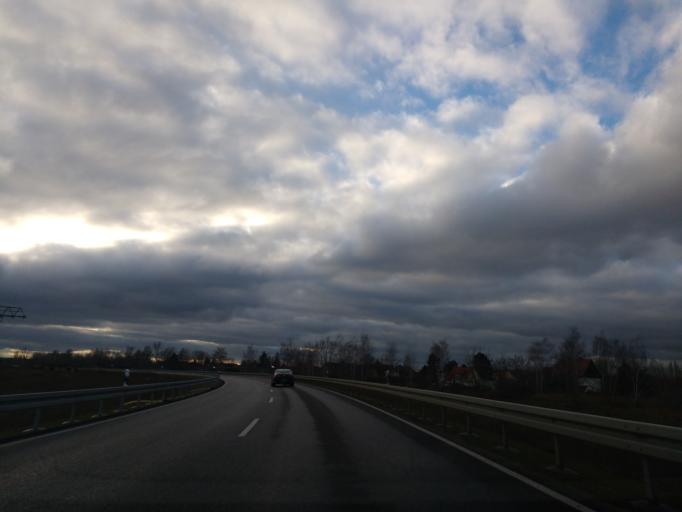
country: DE
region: Saxony-Anhalt
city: Zscherben
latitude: 51.3288
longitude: 11.9833
